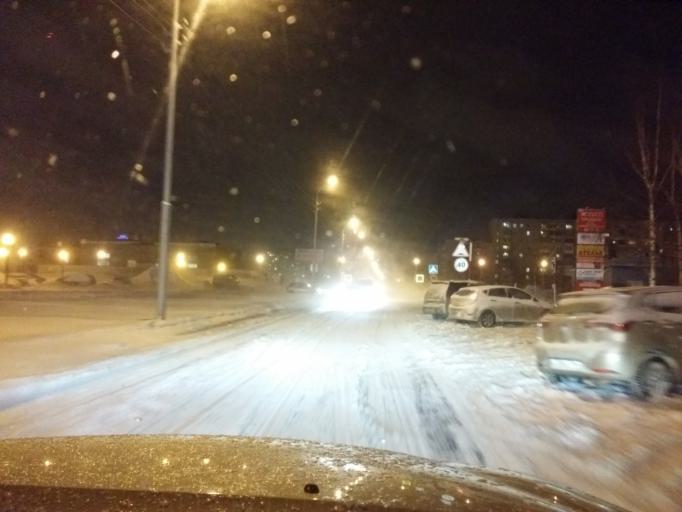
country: RU
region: Khanty-Mansiyskiy Avtonomnyy Okrug
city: Nizhnevartovsk
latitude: 60.9410
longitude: 76.5954
